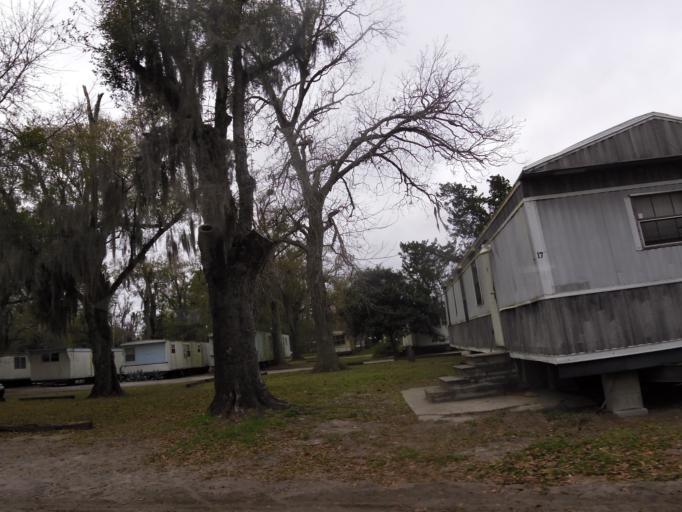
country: US
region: Florida
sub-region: Duval County
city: Jacksonville
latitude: 30.3643
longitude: -81.7178
